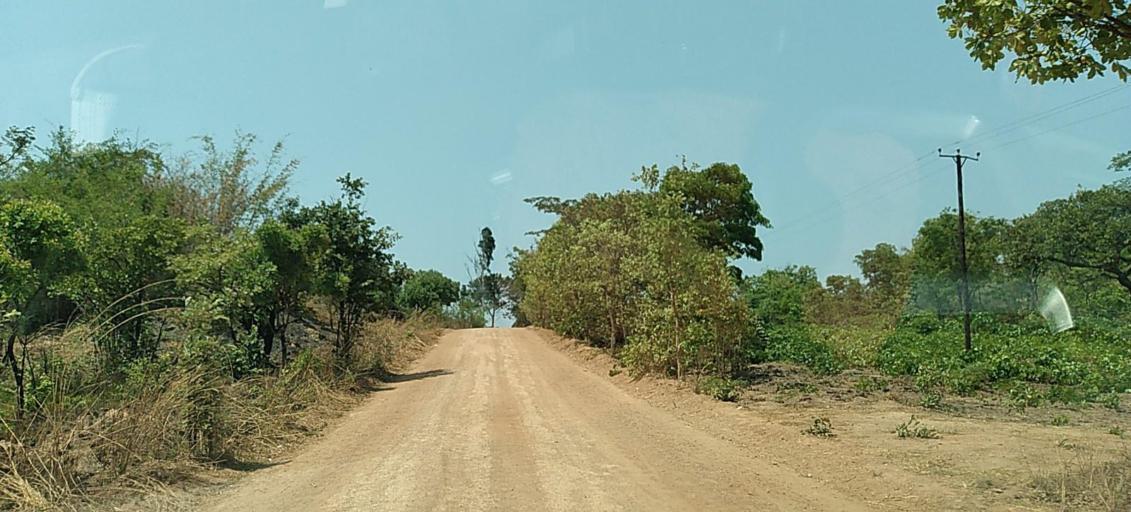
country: ZM
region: Copperbelt
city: Chambishi
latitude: -12.6197
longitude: 27.9553
